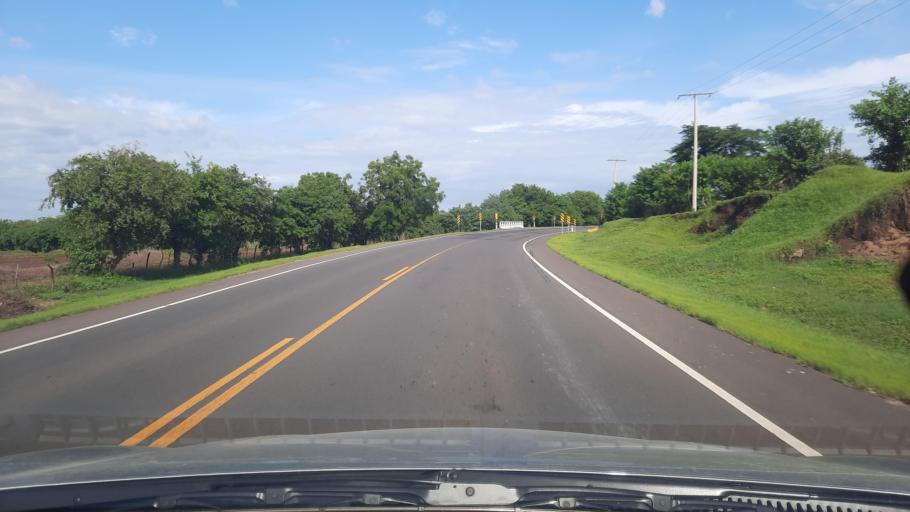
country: NI
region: Chinandega
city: Chichigalpa
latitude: 12.7633
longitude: -86.9010
